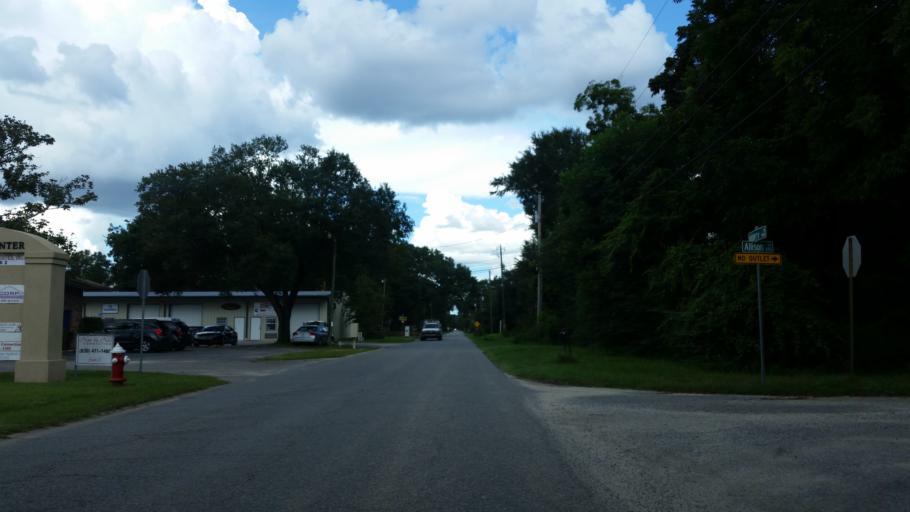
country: US
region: Florida
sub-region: Escambia County
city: Ensley
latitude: 30.5344
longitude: -87.2666
